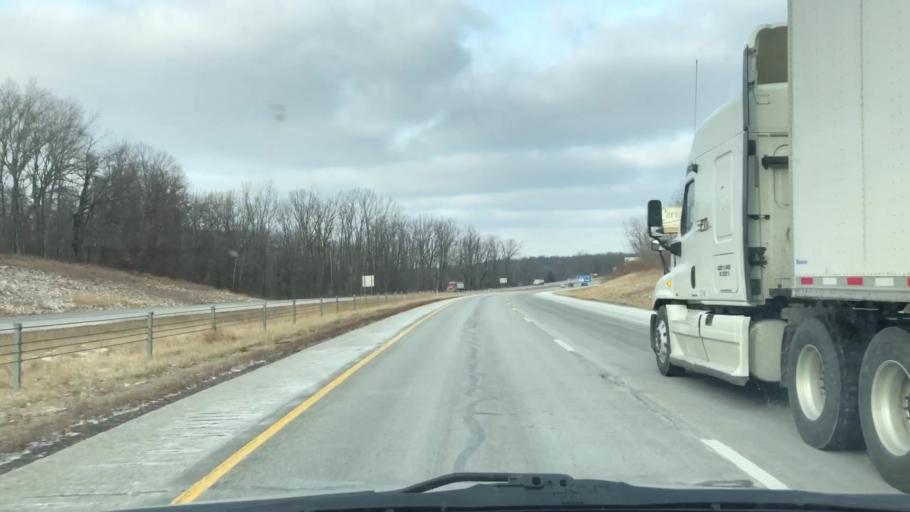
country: US
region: Indiana
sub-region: Steuben County
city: Angola
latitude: 41.6412
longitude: -85.0479
